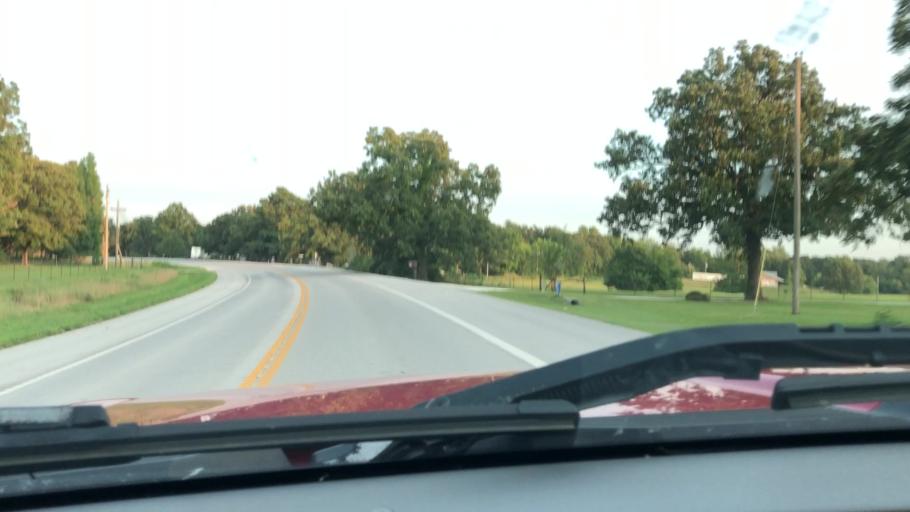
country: US
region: Missouri
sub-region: Jasper County
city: Duquesne
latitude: 36.9777
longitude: -94.4633
